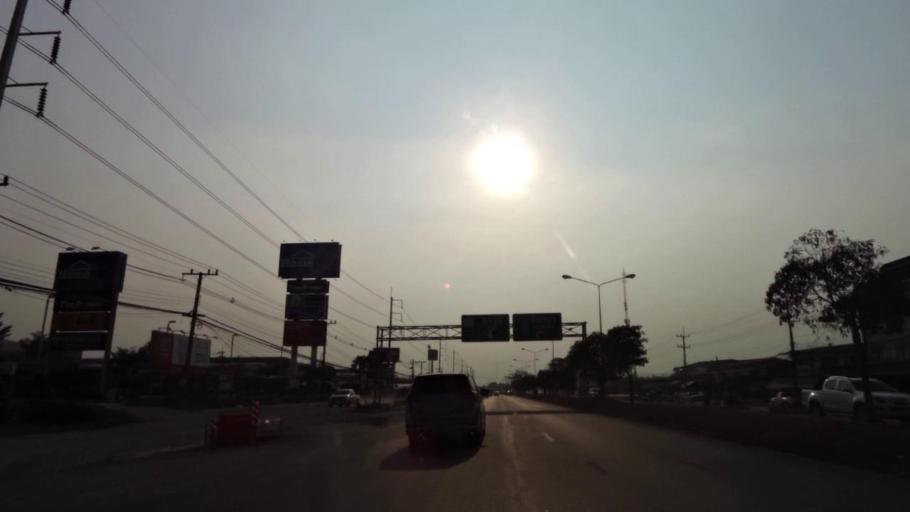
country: TH
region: Chanthaburi
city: Chanthaburi
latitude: 12.6179
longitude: 102.1440
